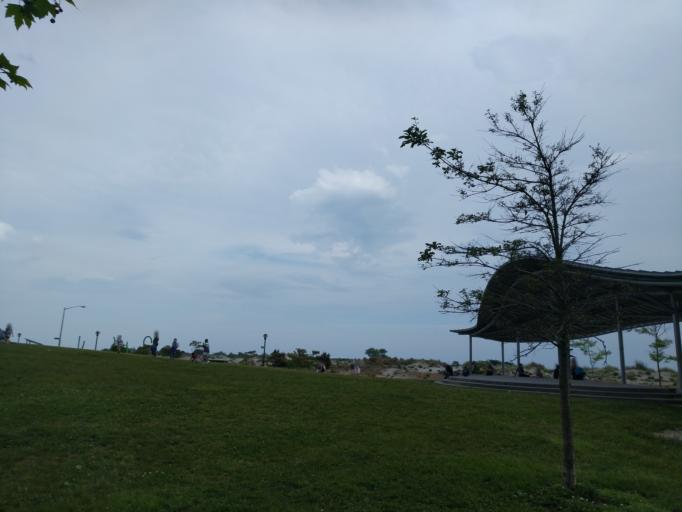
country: US
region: New York
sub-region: Nassau County
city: Atlantic Beach
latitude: 40.5945
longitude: -73.7501
